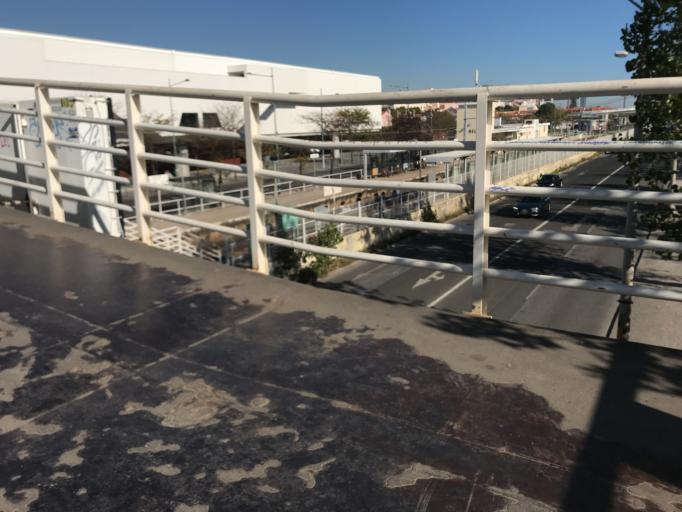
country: PT
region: Setubal
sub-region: Almada
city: Caparica
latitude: 38.6959
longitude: -9.1987
